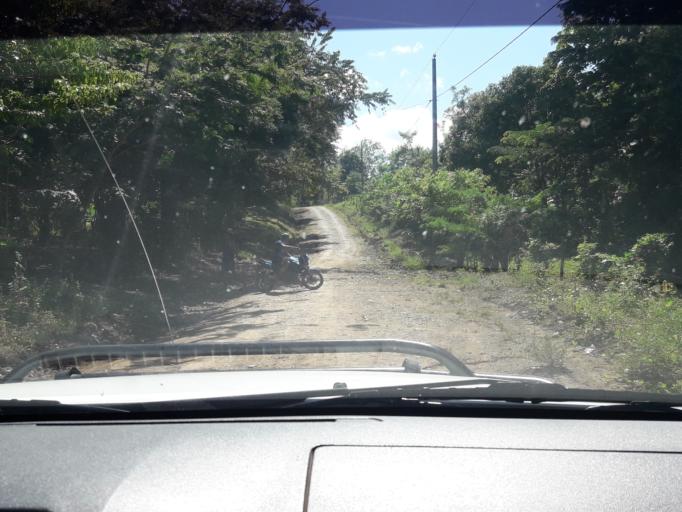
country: NI
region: Rivas
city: Cardenas
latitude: 11.2250
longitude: -85.6497
